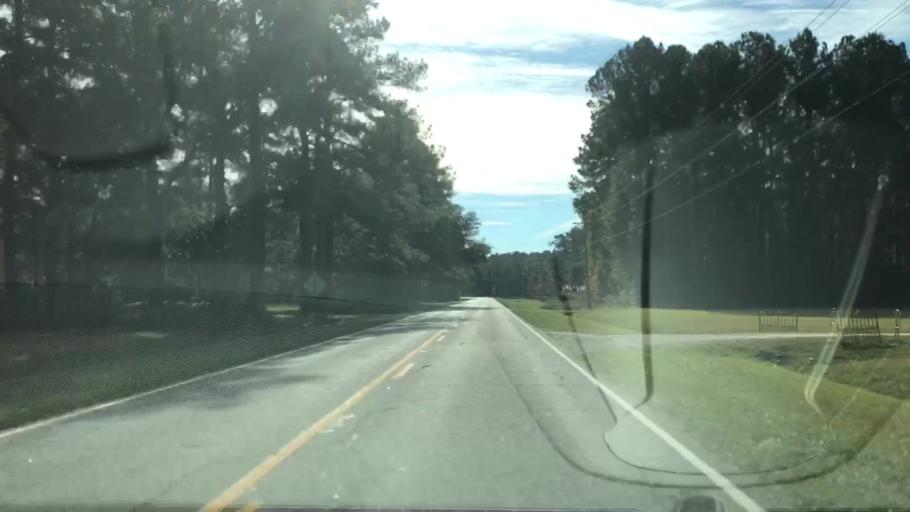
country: US
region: South Carolina
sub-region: Colleton County
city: Walterboro
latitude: 32.8689
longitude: -80.6128
